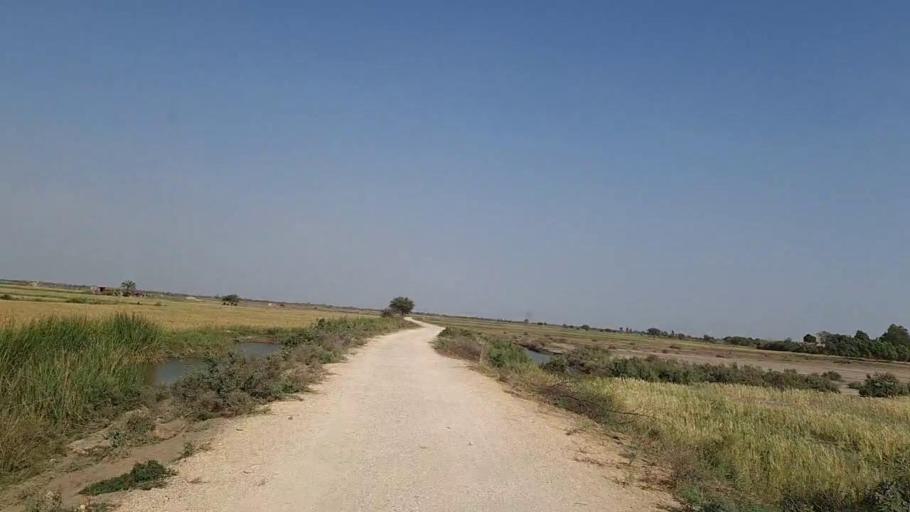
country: PK
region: Sindh
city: Daro Mehar
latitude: 24.7591
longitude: 68.1611
